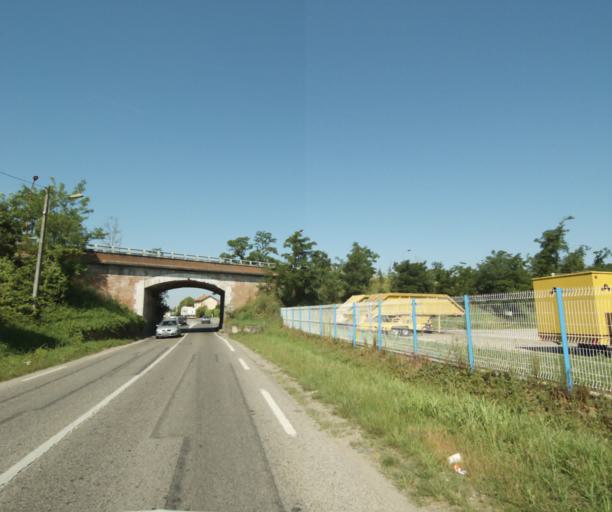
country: FR
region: Midi-Pyrenees
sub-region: Departement du Tarn-et-Garonne
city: Montauban
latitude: 44.0189
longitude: 1.3253
